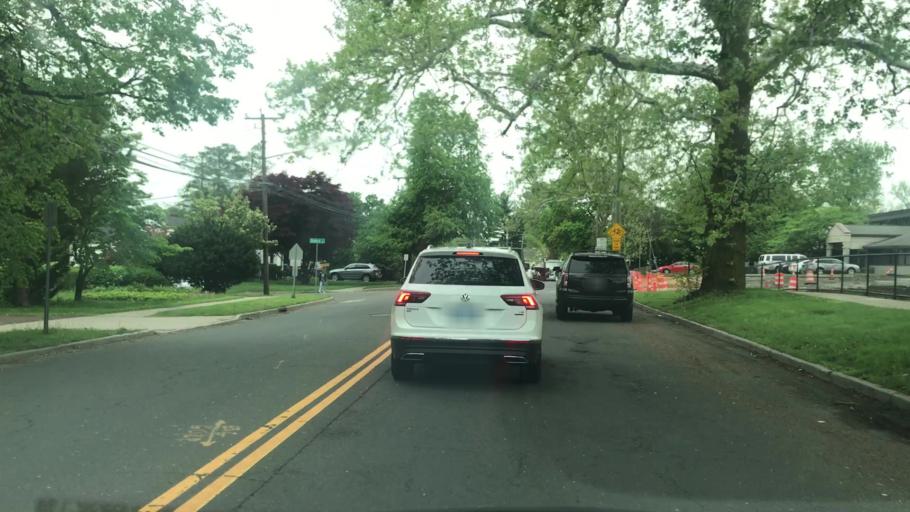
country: US
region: Connecticut
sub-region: Fairfield County
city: Stamford
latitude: 41.0545
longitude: -73.5578
